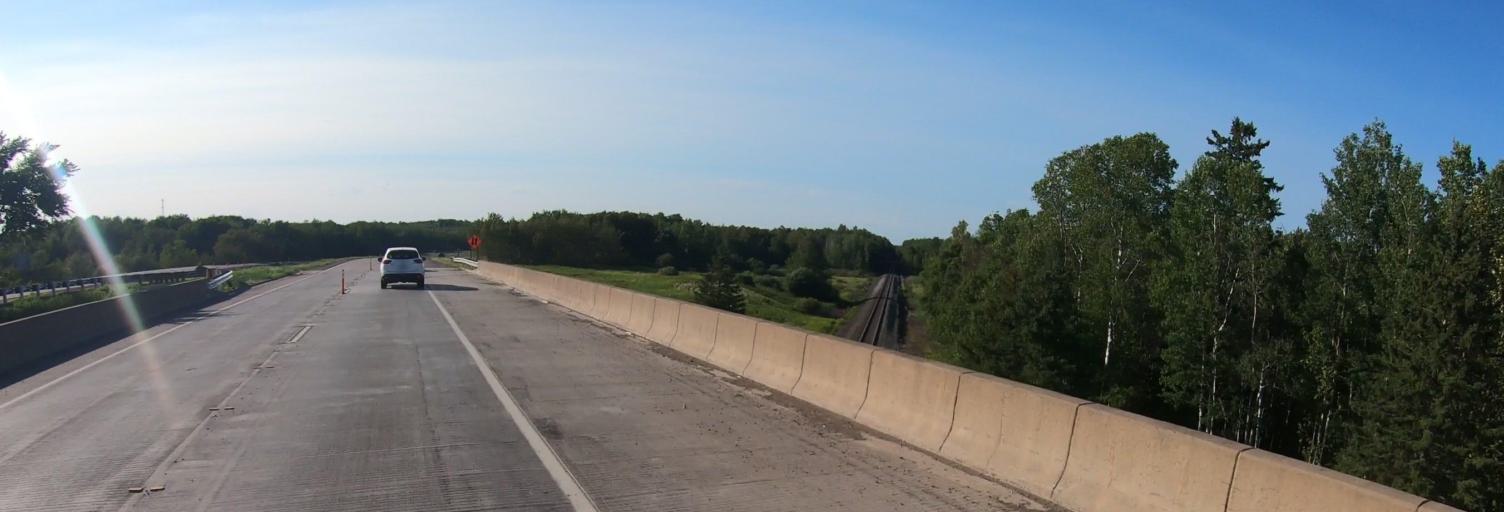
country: US
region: Minnesota
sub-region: Saint Louis County
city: Hermantown
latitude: 46.8794
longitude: -92.3471
